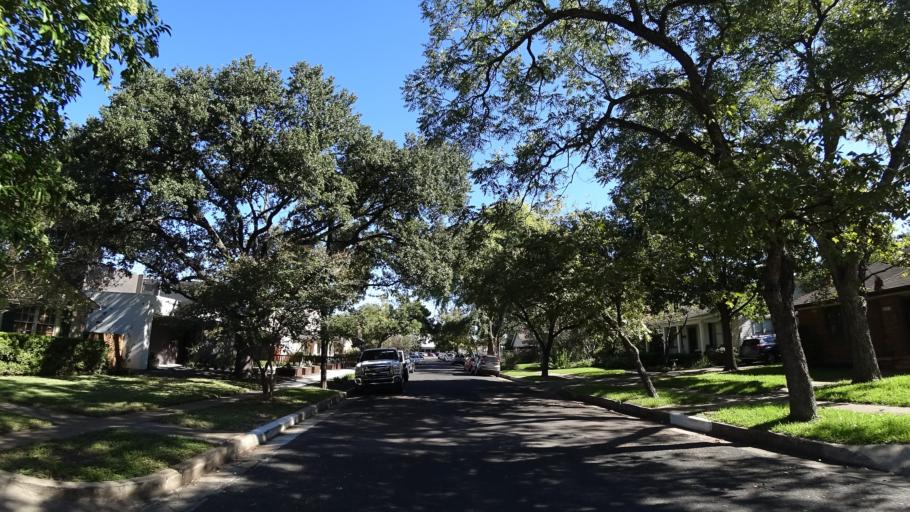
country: US
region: Texas
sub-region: Travis County
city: Austin
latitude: 30.2410
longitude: -97.7538
